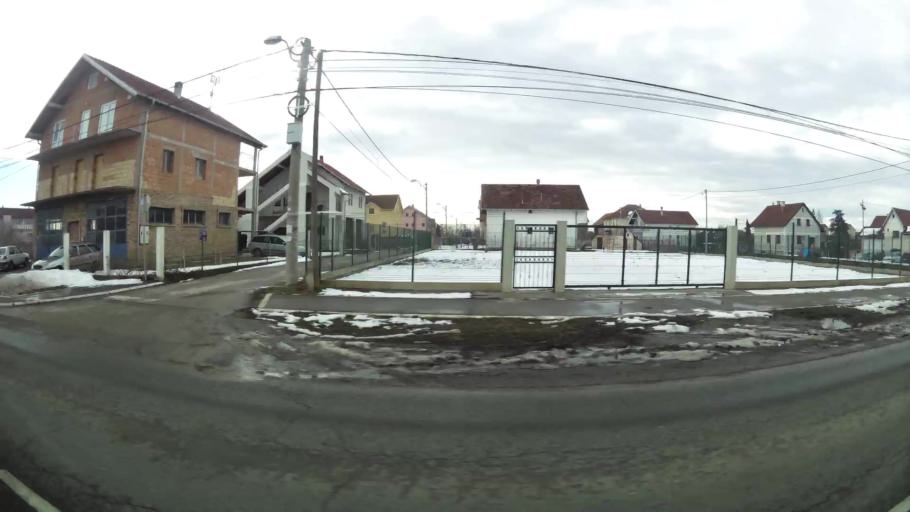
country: RS
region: Central Serbia
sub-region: Belgrade
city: Surcin
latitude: 44.7973
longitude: 20.3116
